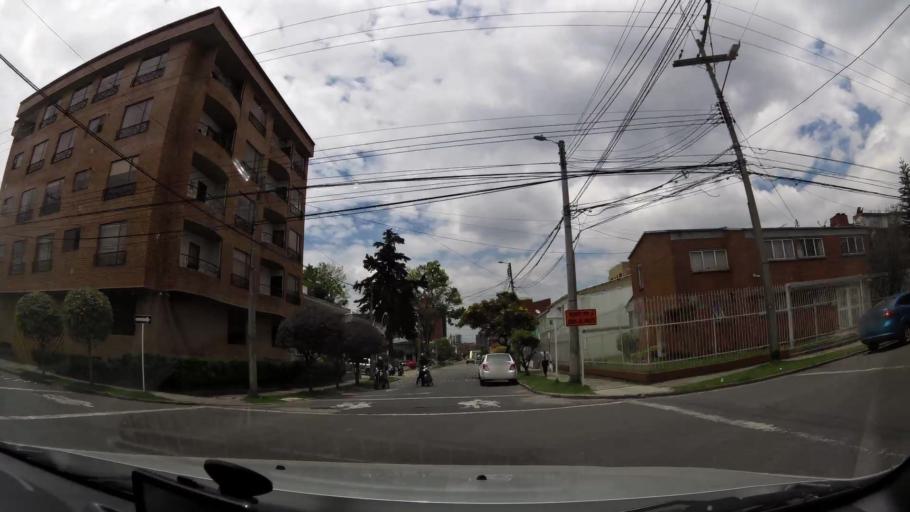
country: CO
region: Bogota D.C.
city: Bogota
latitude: 4.6334
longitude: -74.0920
